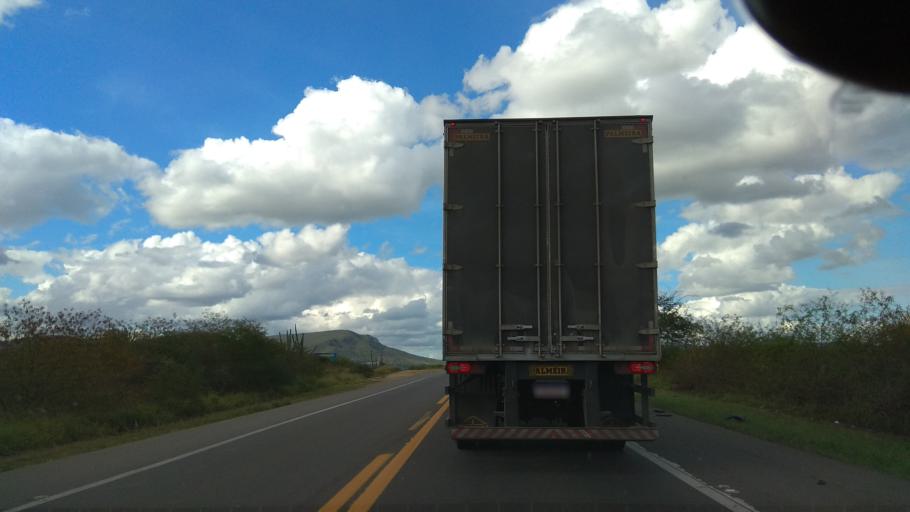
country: BR
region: Bahia
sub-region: Castro Alves
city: Castro Alves
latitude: -12.6750
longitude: -39.6593
